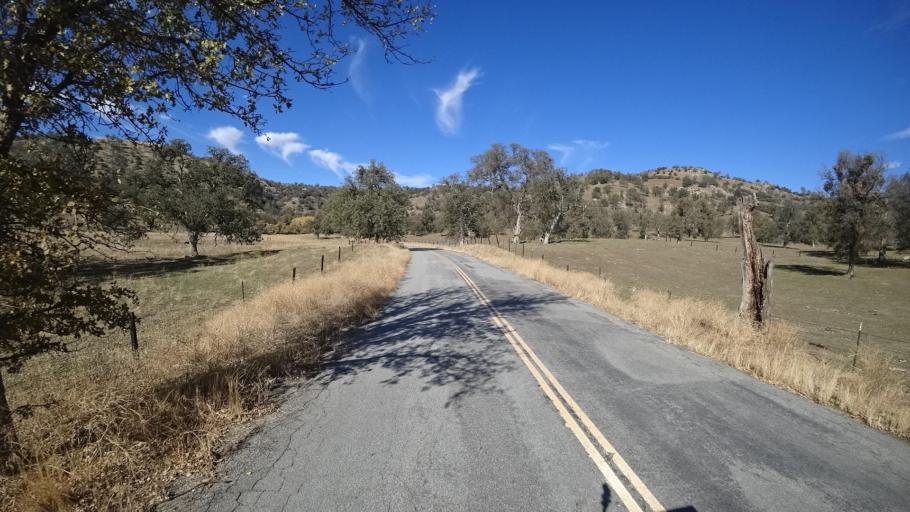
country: US
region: California
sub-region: Kern County
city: Alta Sierra
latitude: 35.6295
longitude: -118.7507
